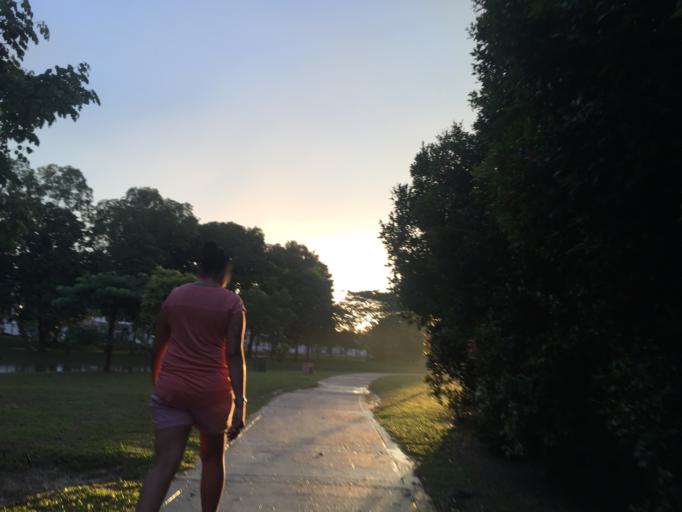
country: MY
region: Selangor
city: Klang
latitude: 2.9881
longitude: 101.4336
